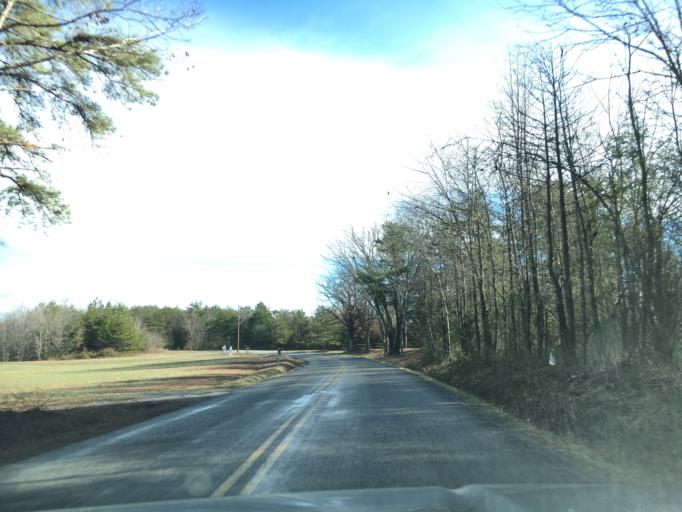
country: US
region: Virginia
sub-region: Amelia County
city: Amelia Court House
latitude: 37.3935
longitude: -78.1074
